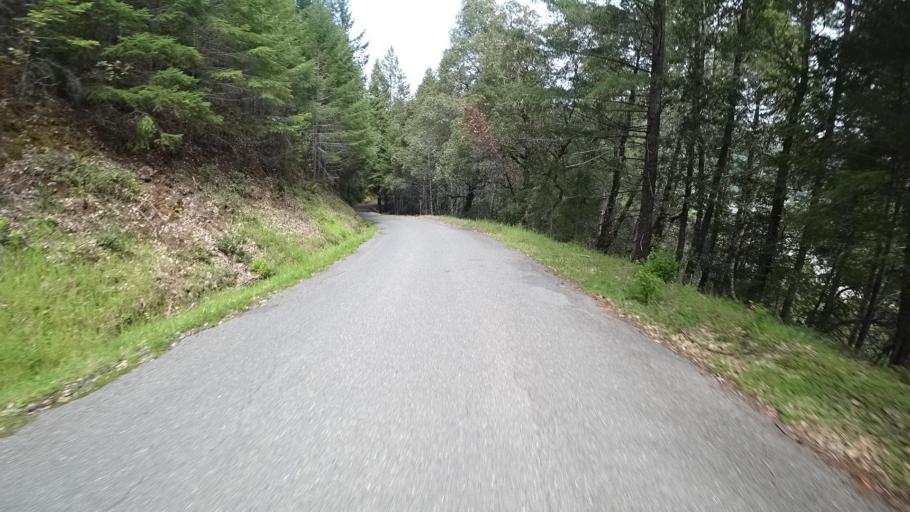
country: US
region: California
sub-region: Humboldt County
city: Redway
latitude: 40.0645
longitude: -123.8288
